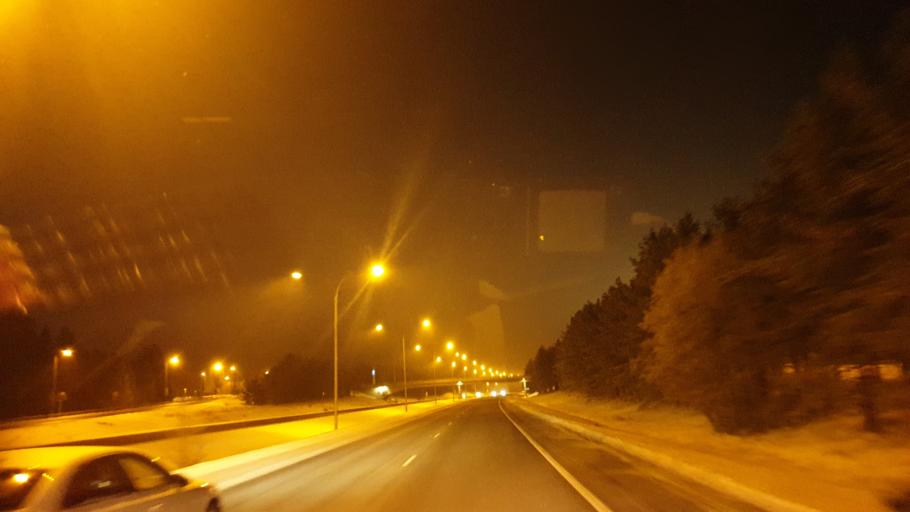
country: FI
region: Northern Ostrobothnia
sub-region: Oulu
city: Kempele
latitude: 64.9431
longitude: 25.5359
